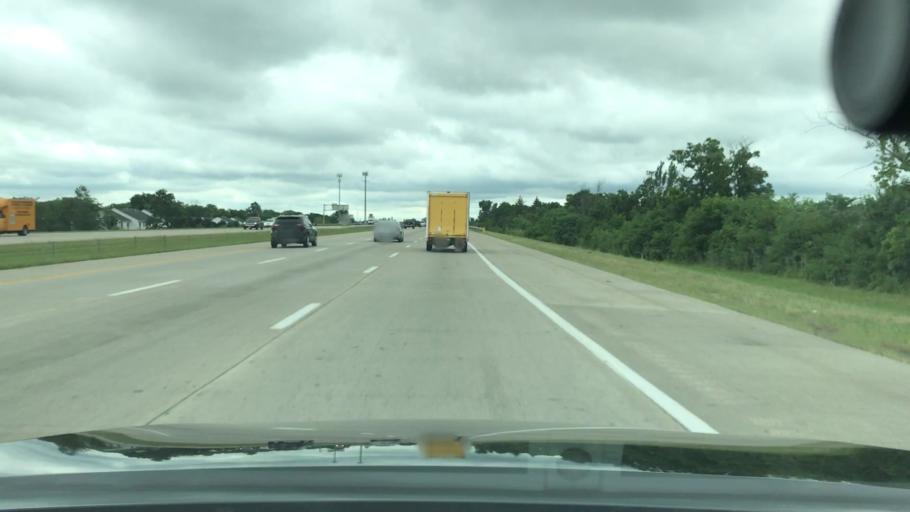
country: US
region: Ohio
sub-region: Franklin County
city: Grove City
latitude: 39.9168
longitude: -83.1128
